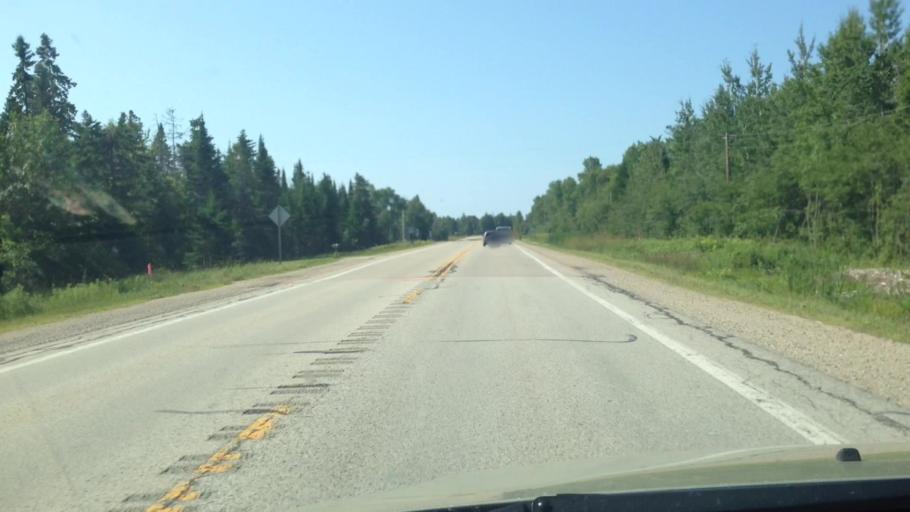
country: US
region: Michigan
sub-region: Delta County
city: Escanaba
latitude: 45.5528
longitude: -87.2693
